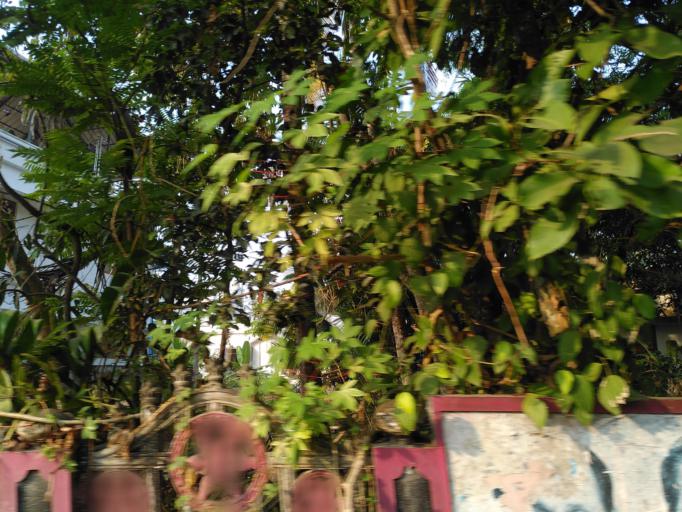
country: IN
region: Kerala
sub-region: Ernakulam
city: Cochin
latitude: 9.9305
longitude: 76.3266
